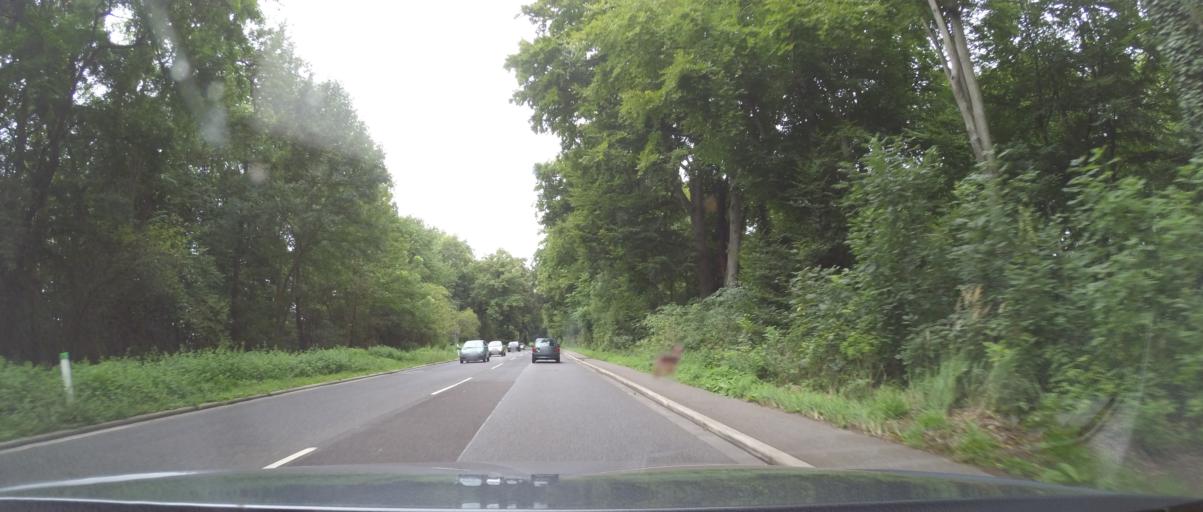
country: DE
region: North Rhine-Westphalia
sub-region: Regierungsbezirk Koln
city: Hurth
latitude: 50.9245
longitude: 6.8853
